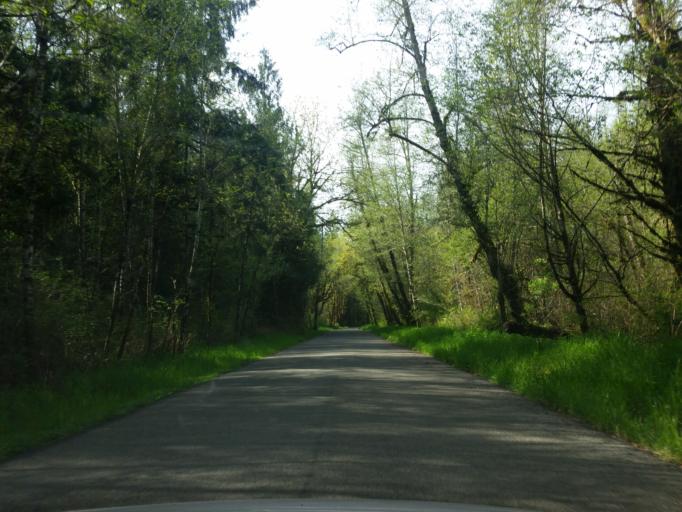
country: US
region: Washington
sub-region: Snohomish County
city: Woods Creek
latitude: 47.9740
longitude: -121.8732
